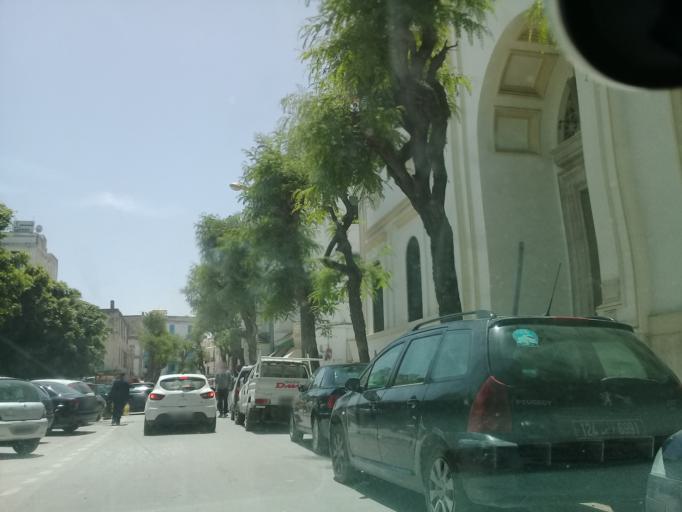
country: TN
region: Tunis
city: Tunis
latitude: 36.7958
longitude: 10.1791
